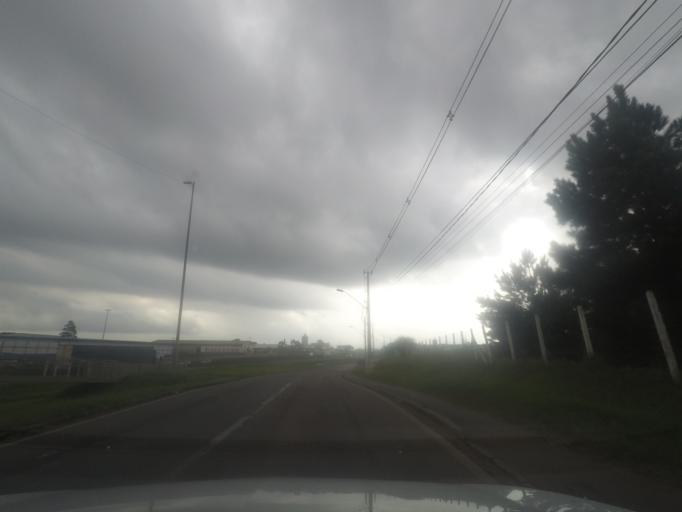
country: BR
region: Parana
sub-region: Sao Jose Dos Pinhais
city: Sao Jose dos Pinhais
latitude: -25.5495
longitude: -49.2824
